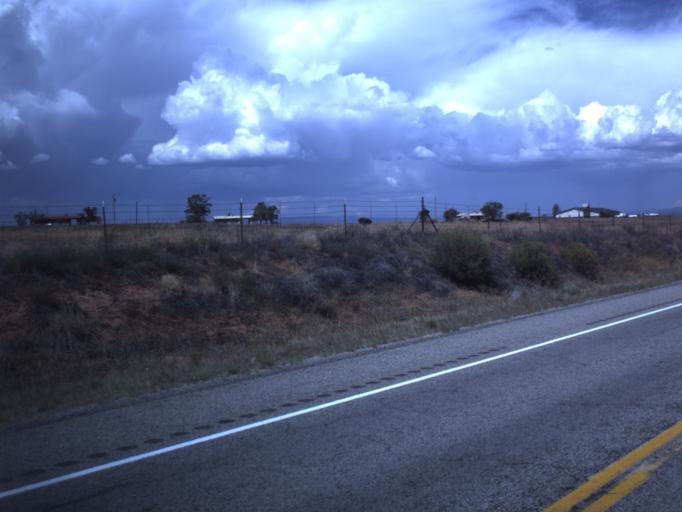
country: US
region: Utah
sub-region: San Juan County
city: Blanding
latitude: 37.4554
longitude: -109.4670
